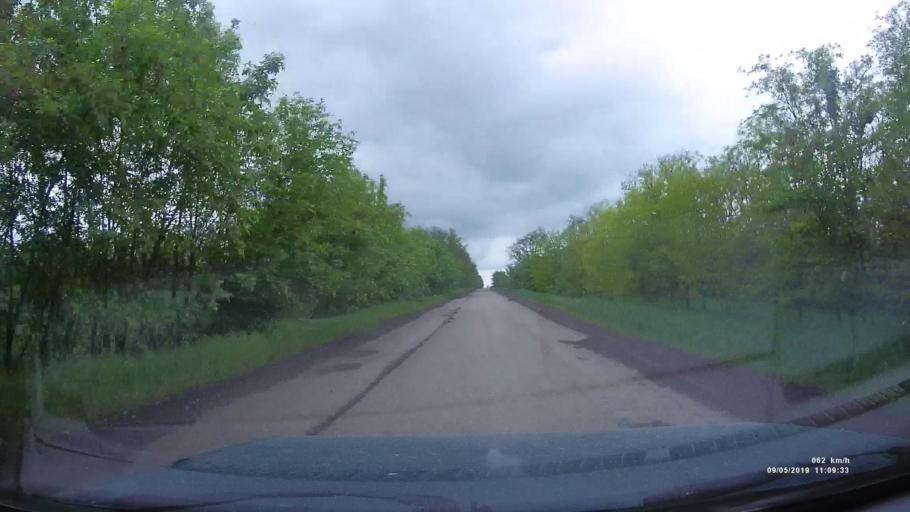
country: RU
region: Krasnodarskiy
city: Kanelovskaya
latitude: 46.7820
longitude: 39.2117
